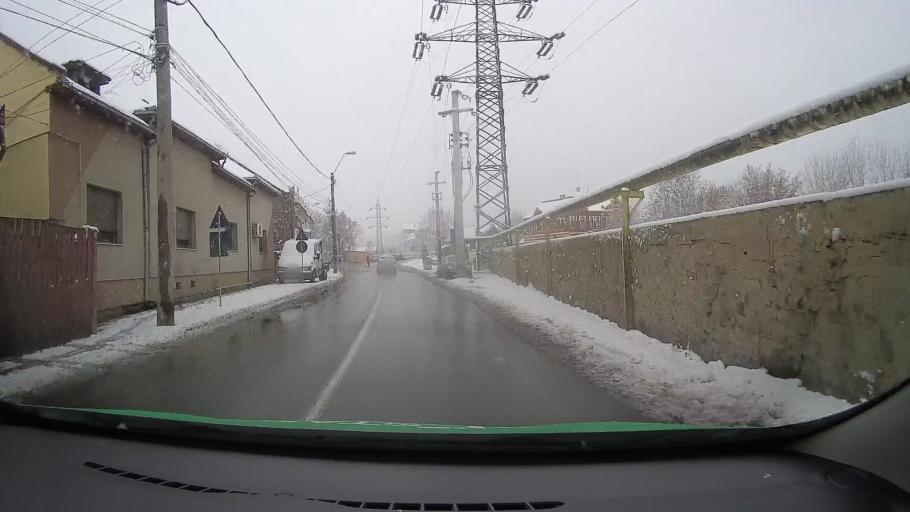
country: RO
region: Hunedoara
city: Hunedoara
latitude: 45.7531
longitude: 22.8946
